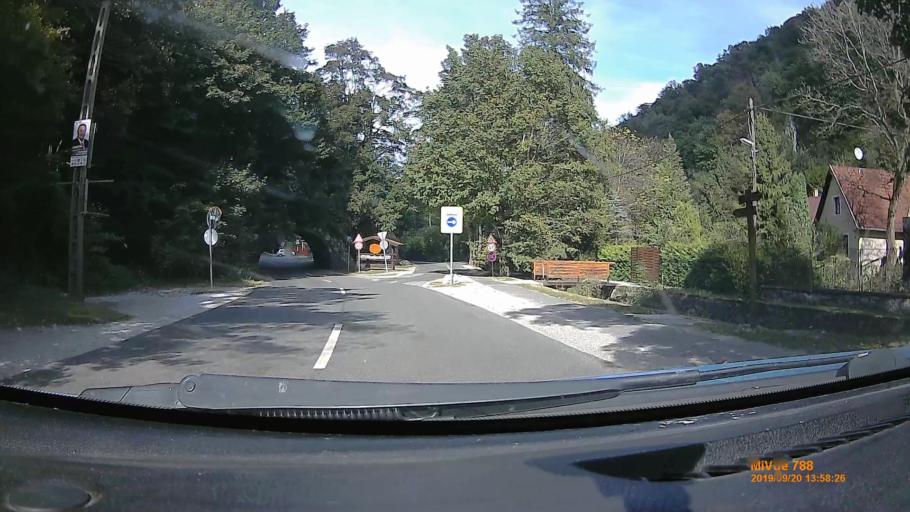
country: HU
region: Borsod-Abauj-Zemplen
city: Sajobabony
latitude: 48.0977
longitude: 20.6211
